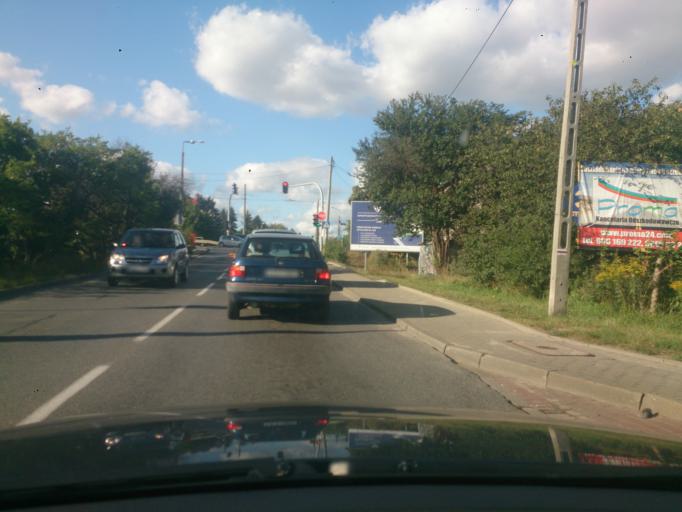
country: PL
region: Pomeranian Voivodeship
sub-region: Gdynia
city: Wielki Kack
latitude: 54.4680
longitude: 18.5091
